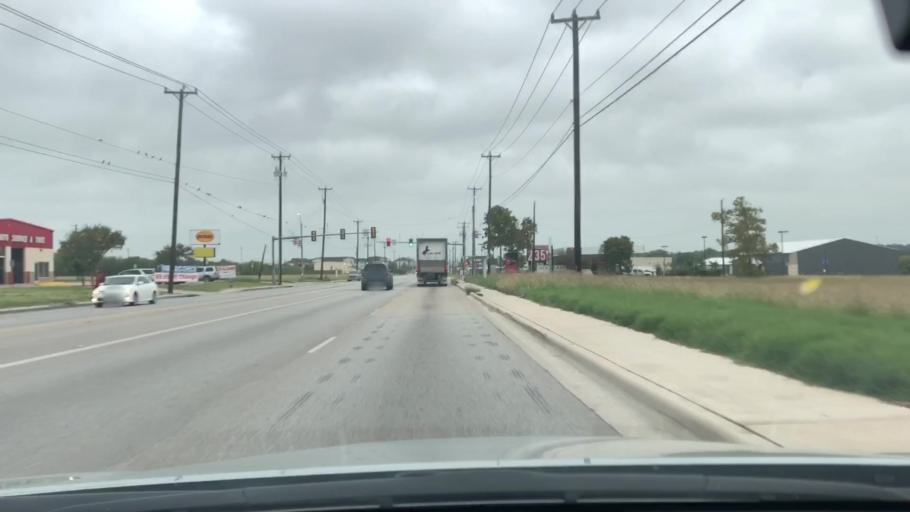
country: US
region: Texas
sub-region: Bexar County
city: Kirby
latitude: 29.4666
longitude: -98.3593
